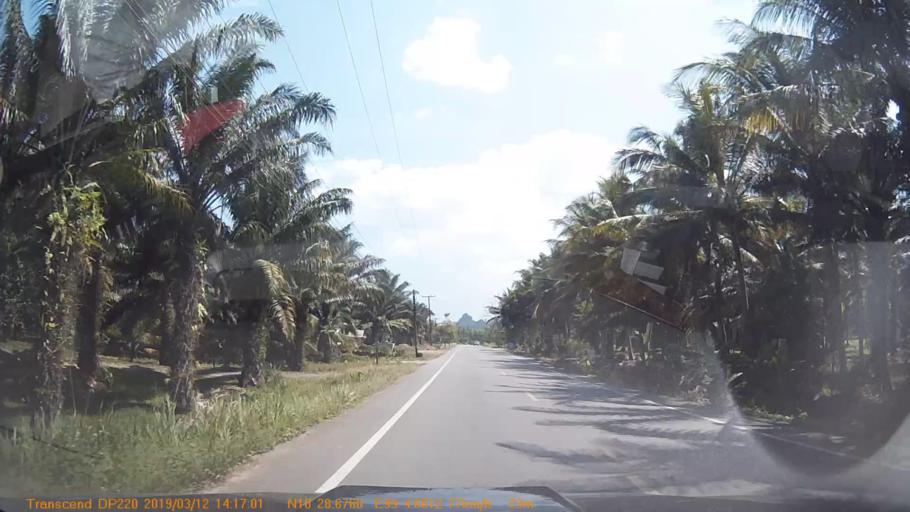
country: TH
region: Chumphon
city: Chumphon
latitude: 10.4776
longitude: 99.0777
